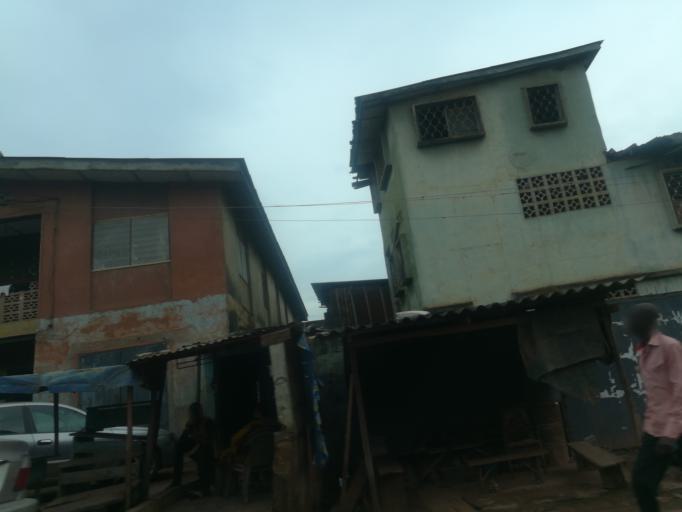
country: NG
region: Oyo
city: Ibadan
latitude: 7.3976
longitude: 3.9233
